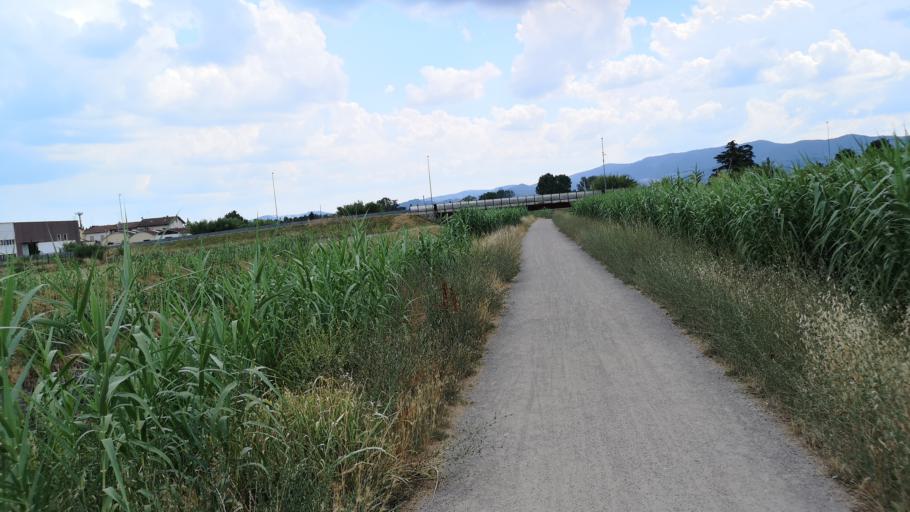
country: IT
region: Tuscany
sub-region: Provincia di Prato
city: Prato
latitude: 43.8801
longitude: 11.0478
